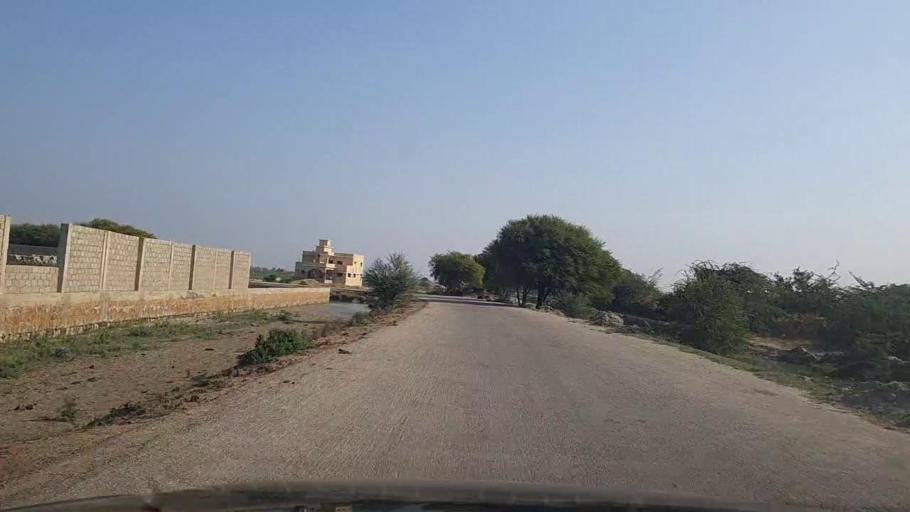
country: PK
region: Sindh
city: Chuhar Jamali
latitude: 24.5889
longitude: 68.0812
